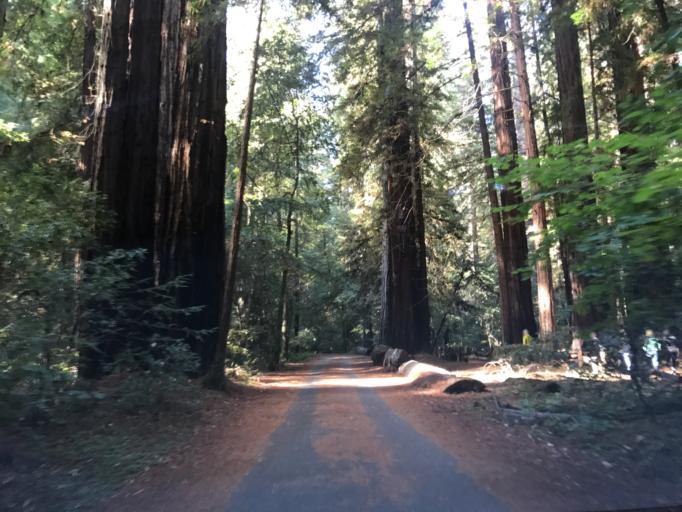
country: US
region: California
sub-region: Sonoma County
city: Guerneville
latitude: 38.5361
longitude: -123.0049
